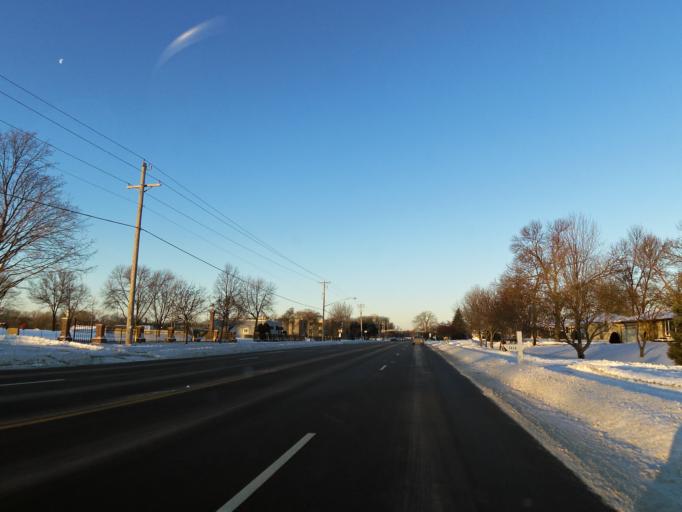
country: US
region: Minnesota
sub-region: Scott County
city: Prior Lake
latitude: 44.7174
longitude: -93.4105
